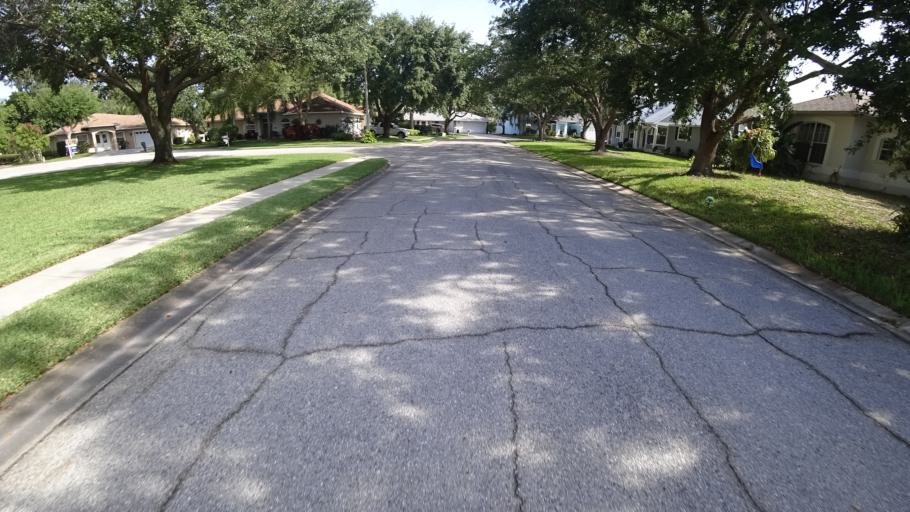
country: US
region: Florida
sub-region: Manatee County
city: West Bradenton
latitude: 27.5135
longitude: -82.6540
